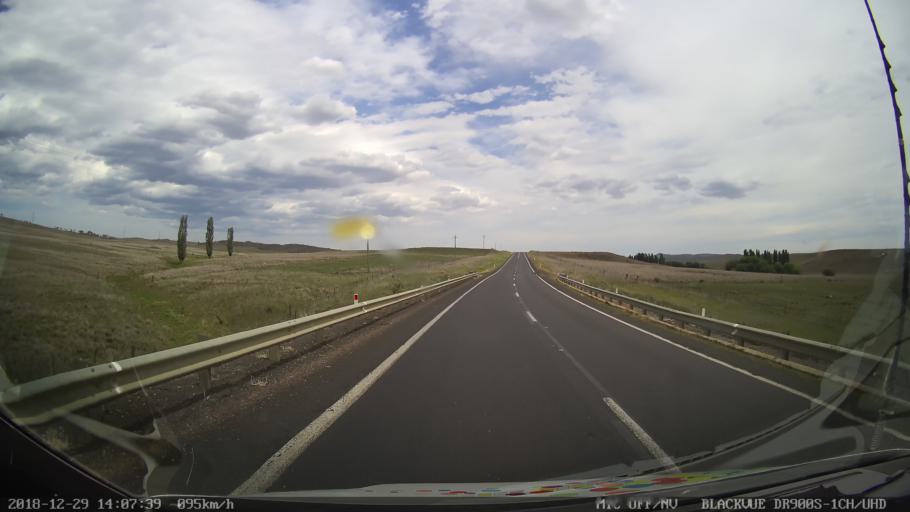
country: AU
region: New South Wales
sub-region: Cooma-Monaro
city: Cooma
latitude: -36.3544
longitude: 149.2150
